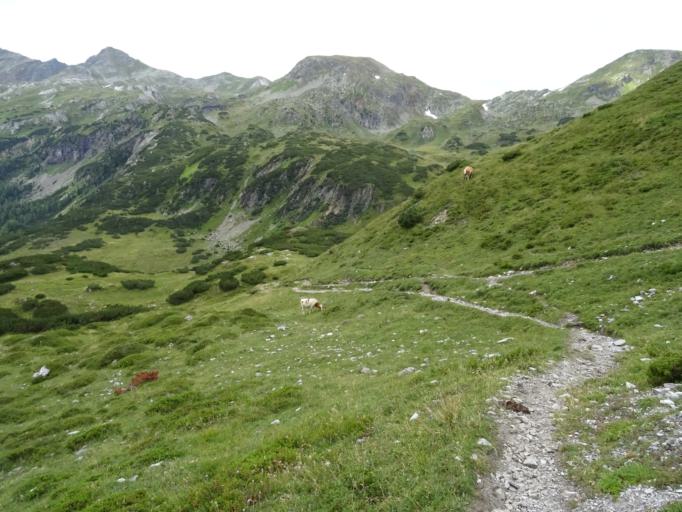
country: AT
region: Salzburg
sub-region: Politischer Bezirk Tamsweg
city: Tweng
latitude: 47.2785
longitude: 13.6067
